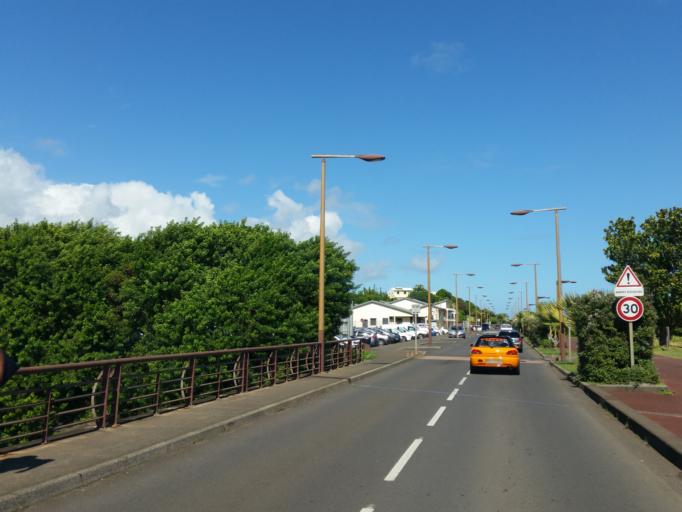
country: RE
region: Reunion
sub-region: Reunion
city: Sainte-Marie
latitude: -20.8959
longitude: 55.5475
